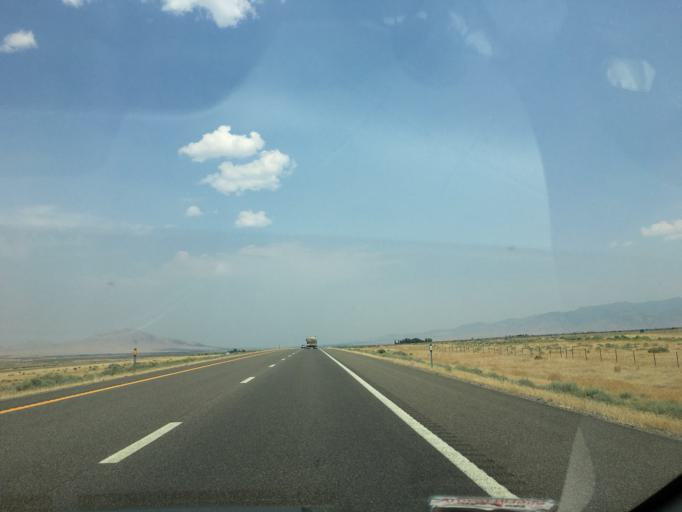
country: US
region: Nevada
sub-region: Humboldt County
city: Winnemucca
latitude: 40.8815
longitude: -117.9253
